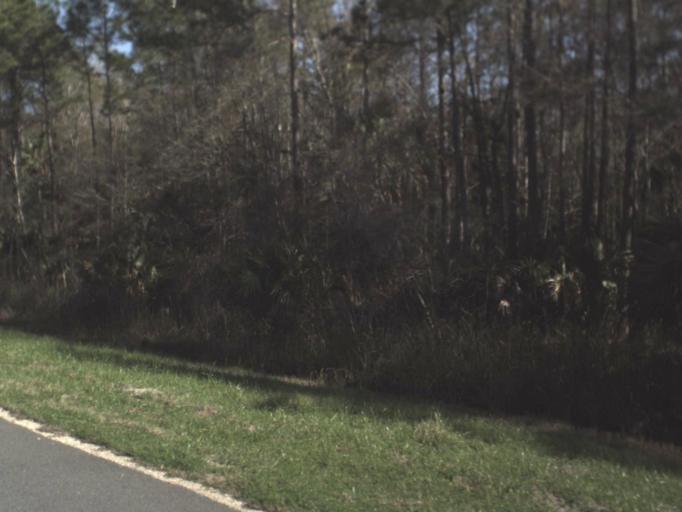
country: US
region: Florida
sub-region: Leon County
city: Woodville
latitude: 30.1667
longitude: -84.0056
